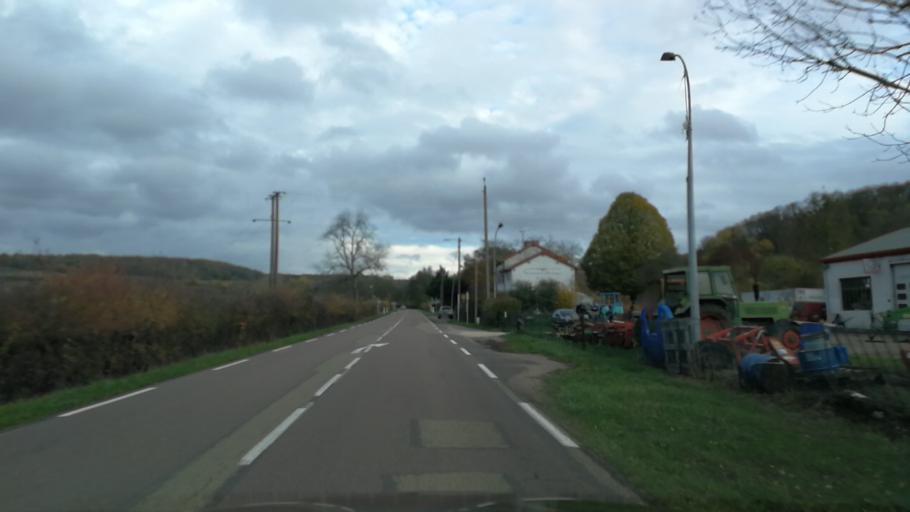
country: FR
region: Bourgogne
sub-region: Departement de la Cote-d'Or
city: Pouilly-en-Auxois
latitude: 47.2691
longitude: 4.3974
